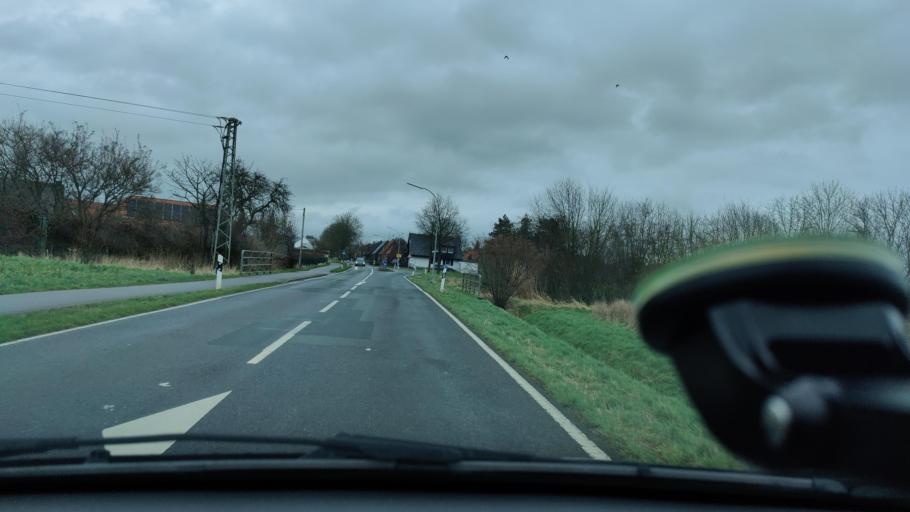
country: DE
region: North Rhine-Westphalia
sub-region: Regierungsbezirk Dusseldorf
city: Kevelaer
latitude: 51.5678
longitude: 6.2839
